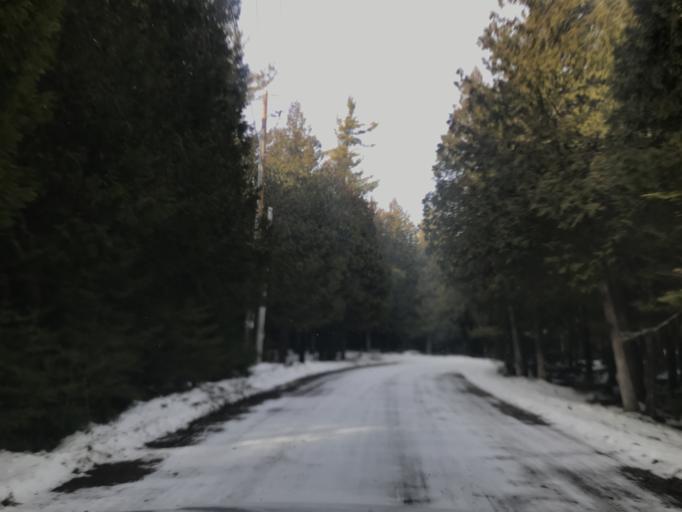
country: US
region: Wisconsin
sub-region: Door County
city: Sturgeon Bay
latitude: 45.1381
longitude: -87.0482
